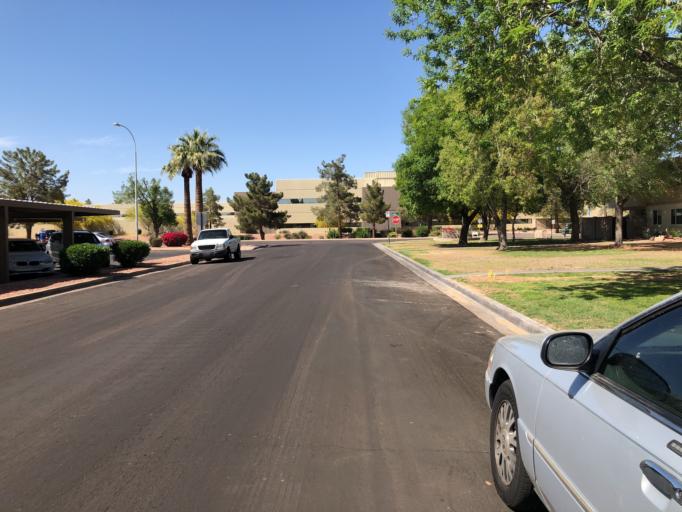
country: US
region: Arizona
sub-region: Maricopa County
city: Tempe
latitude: 33.4579
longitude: -111.9048
